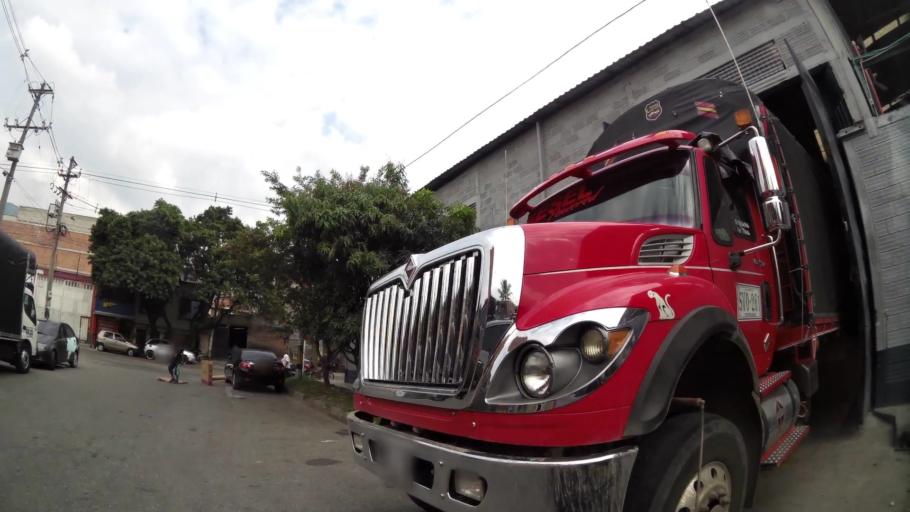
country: CO
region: Antioquia
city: Medellin
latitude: 6.2626
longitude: -75.5703
